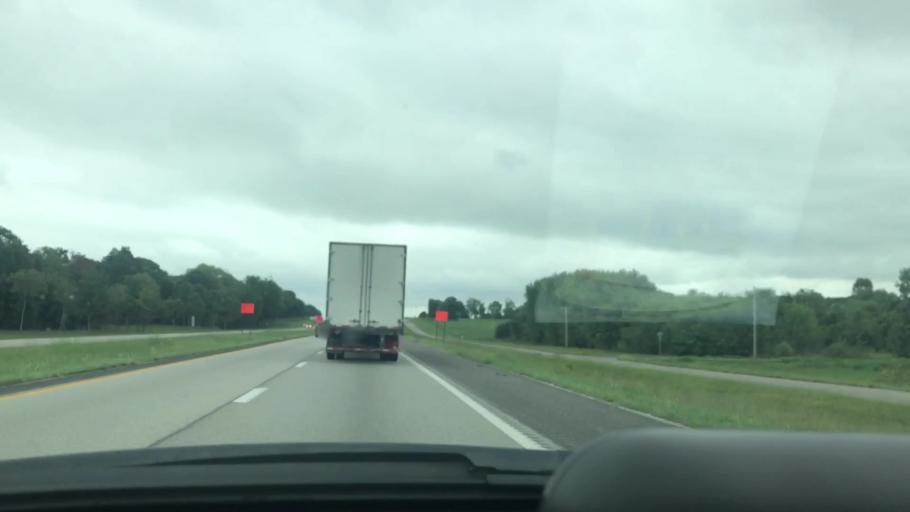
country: US
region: Missouri
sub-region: Greene County
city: Republic
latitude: 37.1858
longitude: -93.5636
